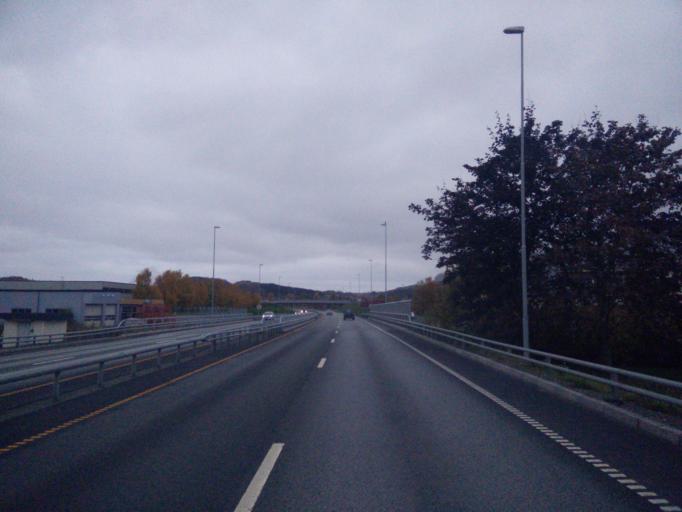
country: NO
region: Nord-Trondelag
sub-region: Stjordal
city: Stjordal
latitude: 63.4769
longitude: 10.9024
